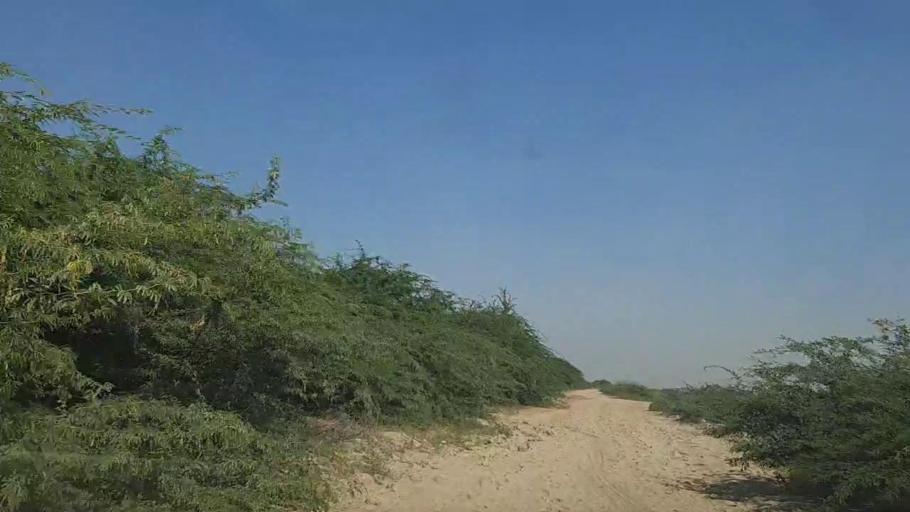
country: PK
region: Sindh
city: Thatta
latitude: 24.8487
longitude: 68.0265
